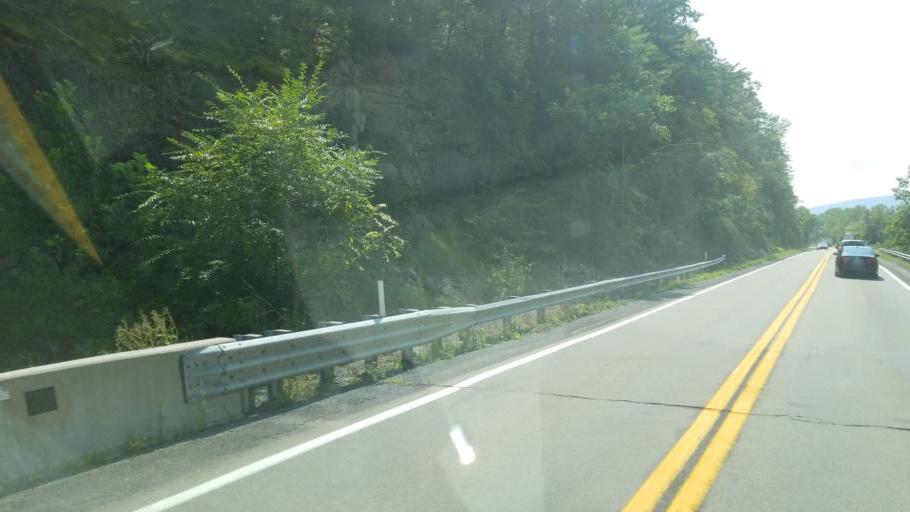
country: US
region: Virginia
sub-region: Frederick County
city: Shawnee Land
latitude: 39.4029
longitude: -78.4180
